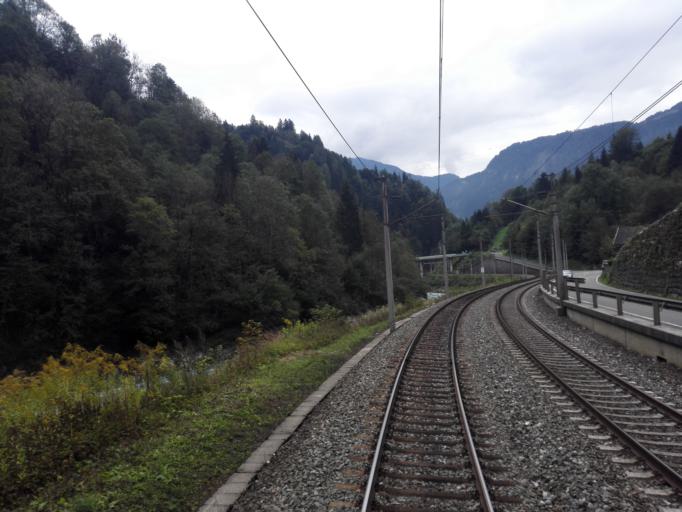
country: AT
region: Salzburg
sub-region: Politischer Bezirk Zell am See
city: Lend
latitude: 47.3065
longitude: 13.0298
